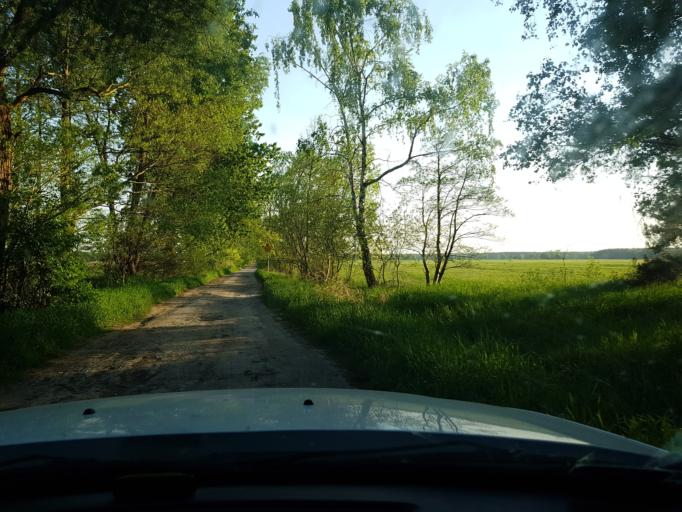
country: PL
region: West Pomeranian Voivodeship
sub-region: Powiat stargardzki
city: Kobylanka
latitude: 53.4090
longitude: 14.8957
